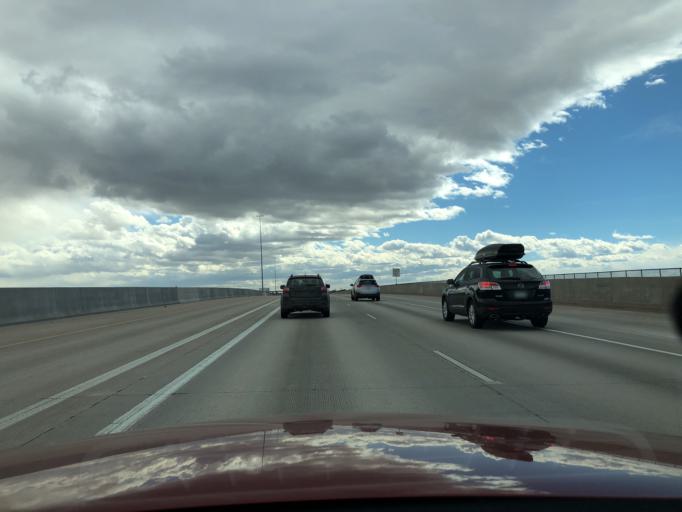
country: US
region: Colorado
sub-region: Broomfield County
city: Broomfield
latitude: 39.8943
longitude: -105.0772
